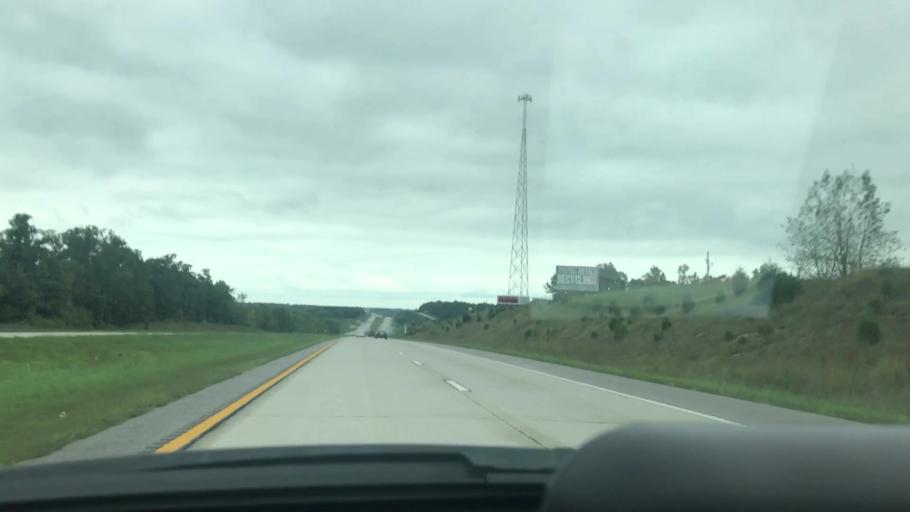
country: US
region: Missouri
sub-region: Greene County
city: Fair Grove
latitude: 37.5075
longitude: -93.1388
